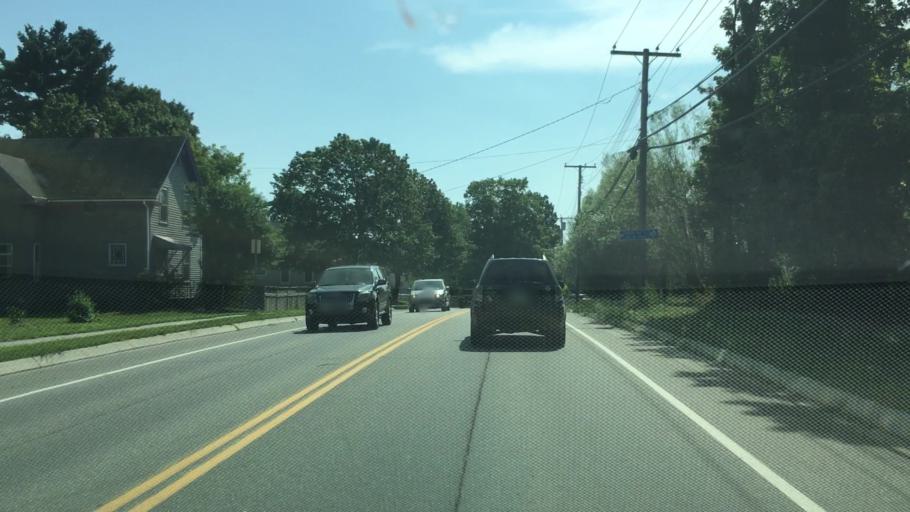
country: US
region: Maine
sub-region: Penobscot County
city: Bangor
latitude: 44.8163
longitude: -68.7650
